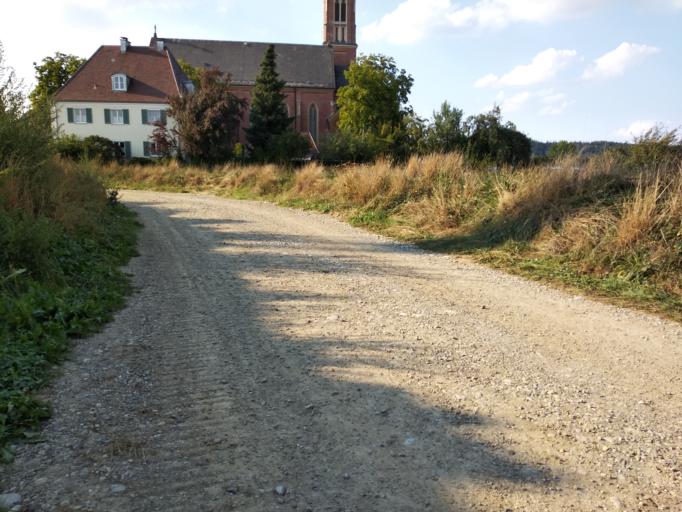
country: DE
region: Bavaria
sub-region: Swabia
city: Westerheim
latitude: 48.0163
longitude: 10.3031
